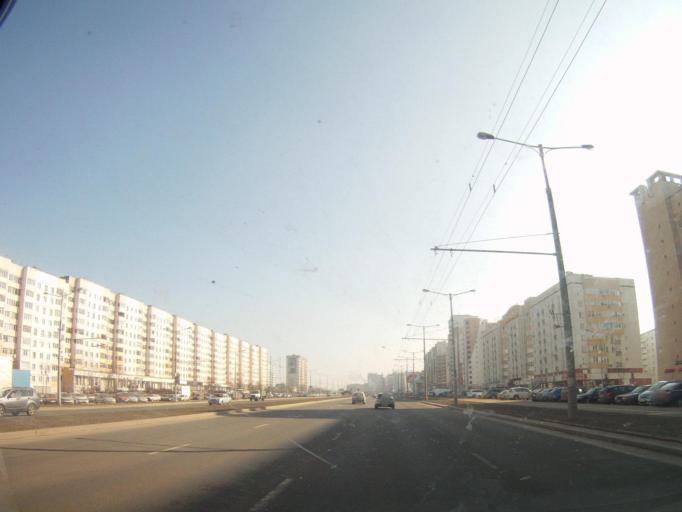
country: BY
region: Minsk
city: Novoye Medvezhino
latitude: 53.9065
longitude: 27.4437
